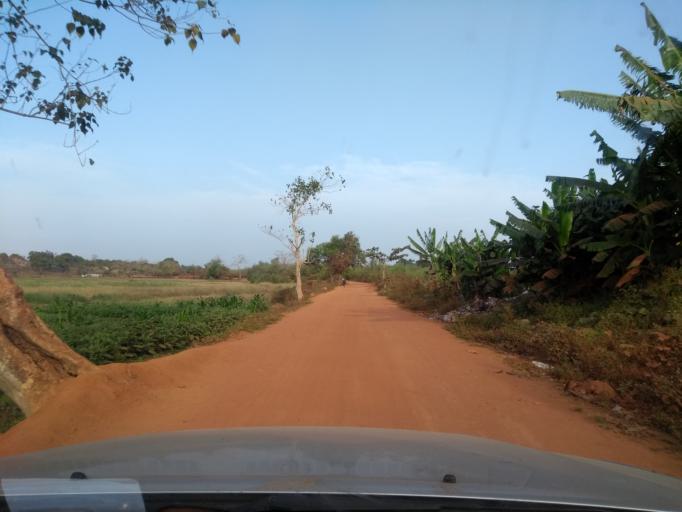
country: GN
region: Kindia
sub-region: Prefecture de Dubreka
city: Dubreka
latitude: 9.7890
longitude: -13.5281
